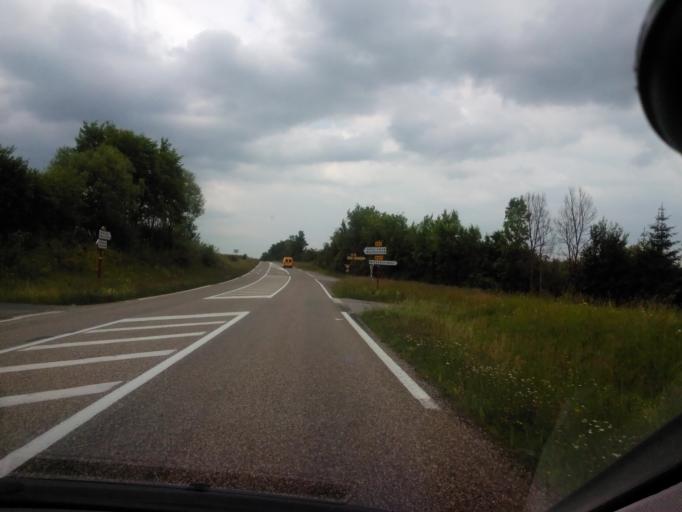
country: FR
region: Alsace
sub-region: Departement du Bas-Rhin
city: Sarrewerden
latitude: 48.8680
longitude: 7.0364
